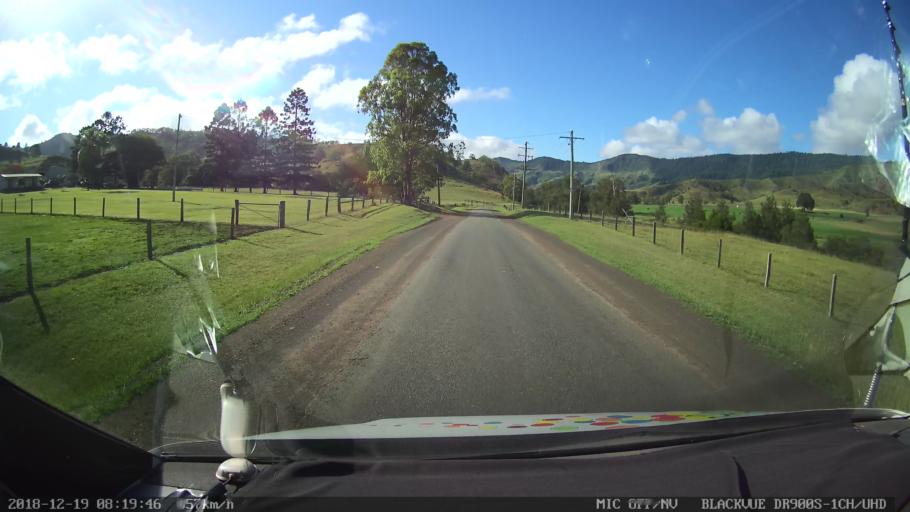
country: AU
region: New South Wales
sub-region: Kyogle
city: Kyogle
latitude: -28.2848
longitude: 152.9097
